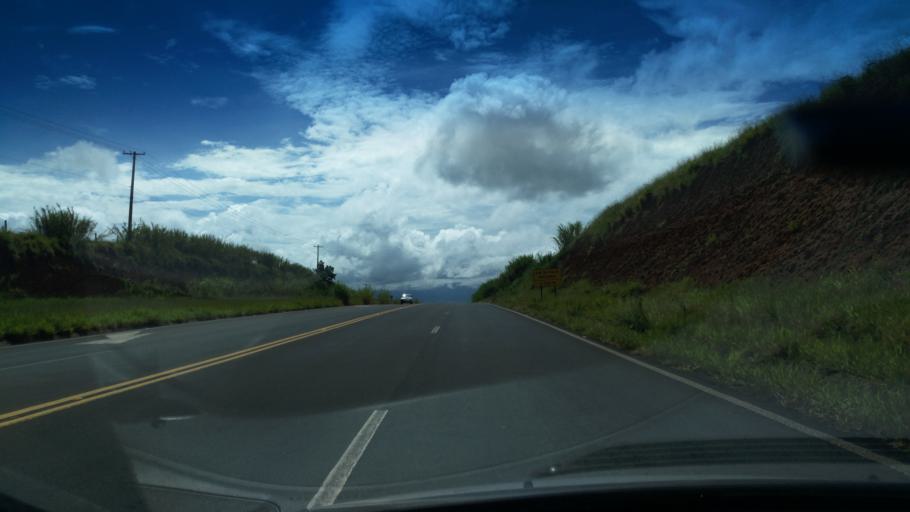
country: BR
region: Sao Paulo
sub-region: Santo Antonio Do Jardim
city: Espirito Santo do Pinhal
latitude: -22.1534
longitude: -46.7232
